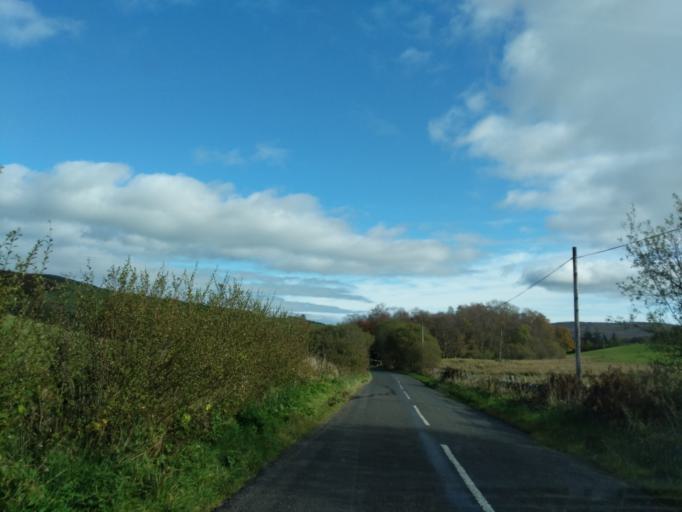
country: GB
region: Scotland
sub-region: Dumfries and Galloway
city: Sanquhar
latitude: 55.1592
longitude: -3.9973
